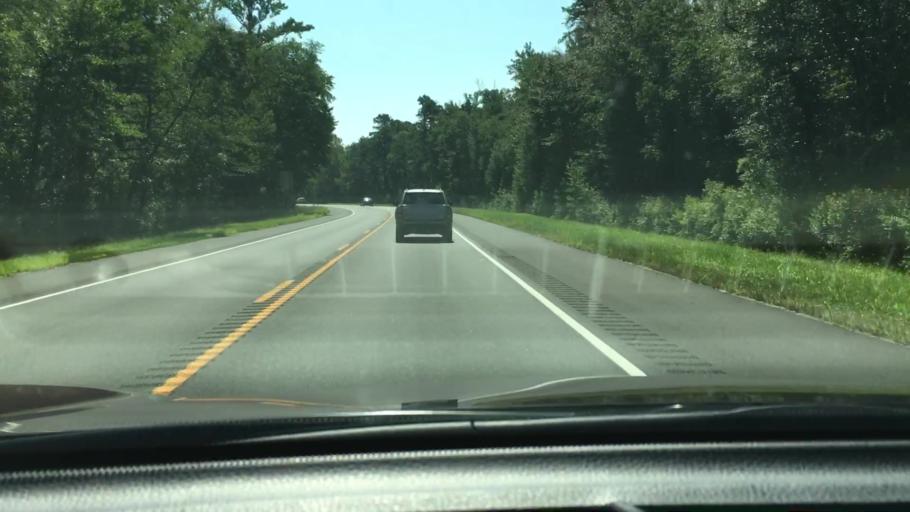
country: US
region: New Jersey
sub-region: Cape May County
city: Woodbine
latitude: 39.3255
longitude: -74.8672
